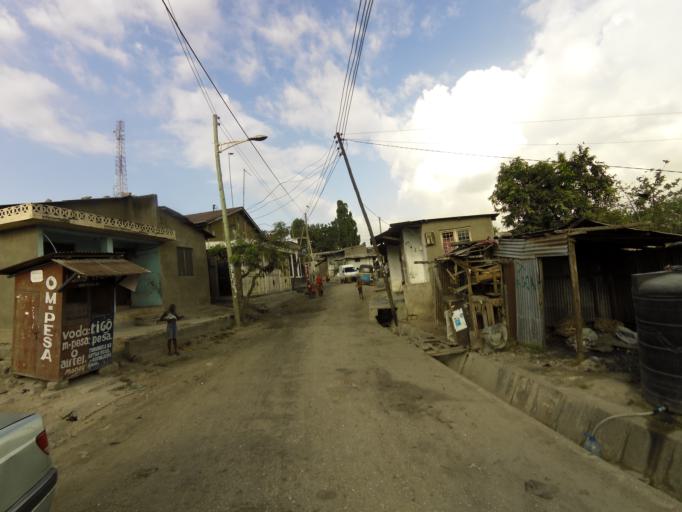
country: TZ
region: Dar es Salaam
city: Magomeni
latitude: -6.7923
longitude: 39.2282
